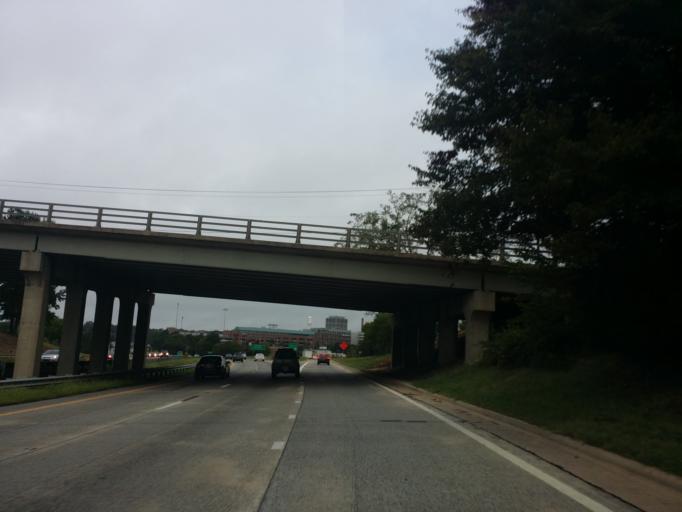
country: US
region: North Carolina
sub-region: Durham County
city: Durham
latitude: 35.9876
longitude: -78.8966
